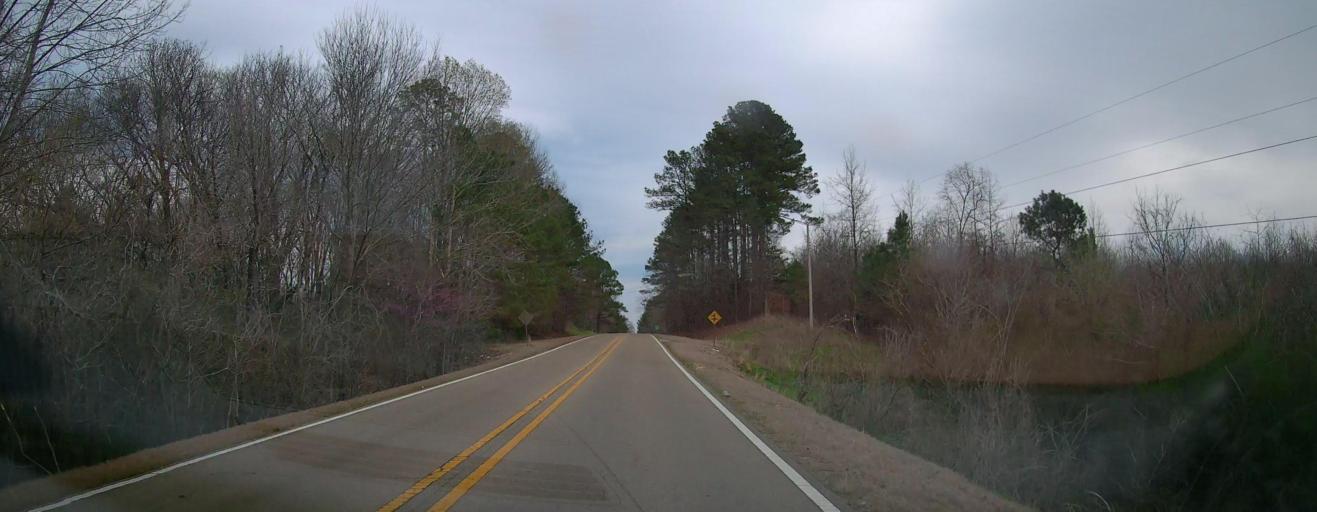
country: US
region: Mississippi
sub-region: Itawamba County
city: Mantachie
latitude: 34.2581
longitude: -88.5075
